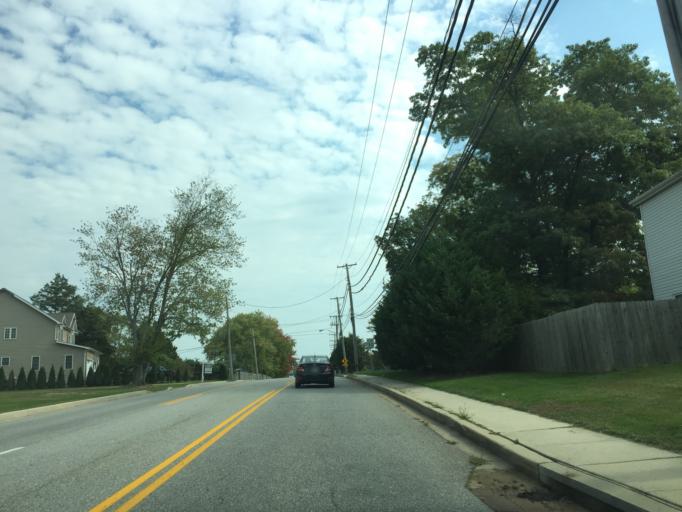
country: US
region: Maryland
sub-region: Harford County
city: Bel Air South
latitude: 39.4788
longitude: -76.3142
